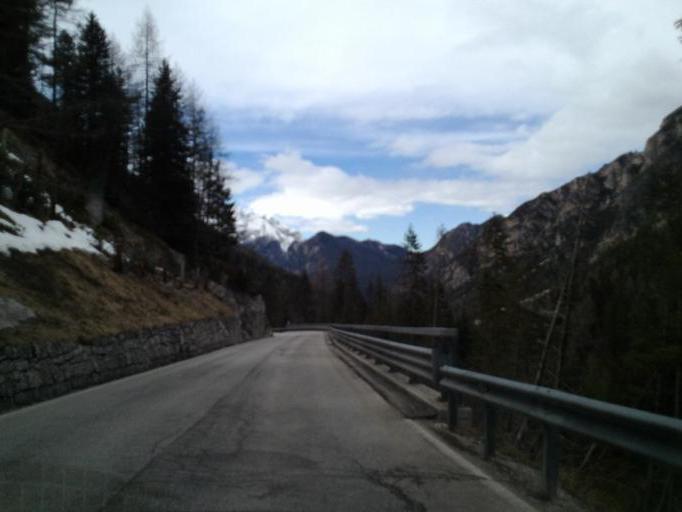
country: IT
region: Veneto
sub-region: Provincia di Belluno
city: Cortina d'Ampezzo
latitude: 46.5995
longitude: 12.2479
